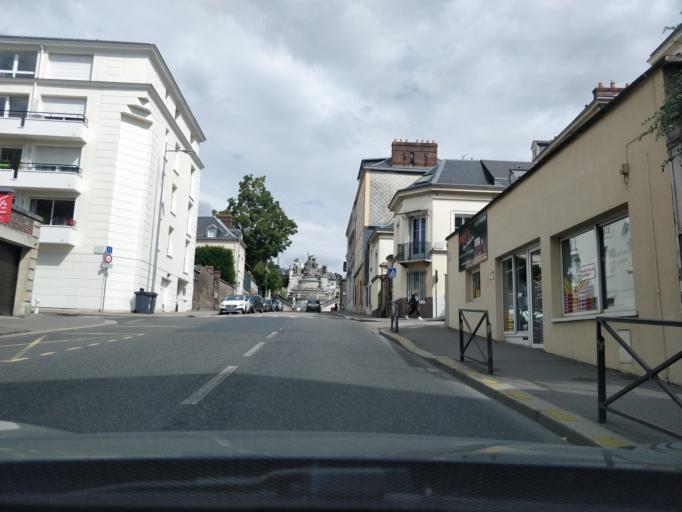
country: FR
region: Haute-Normandie
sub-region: Departement de la Seine-Maritime
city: Rouen
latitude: 49.4459
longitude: 1.1001
